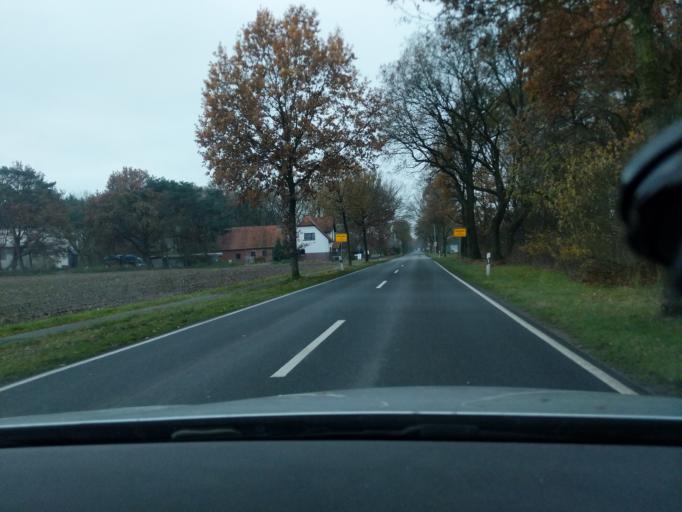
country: DE
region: Lower Saxony
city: Heeslingen
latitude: 53.3233
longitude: 9.3474
